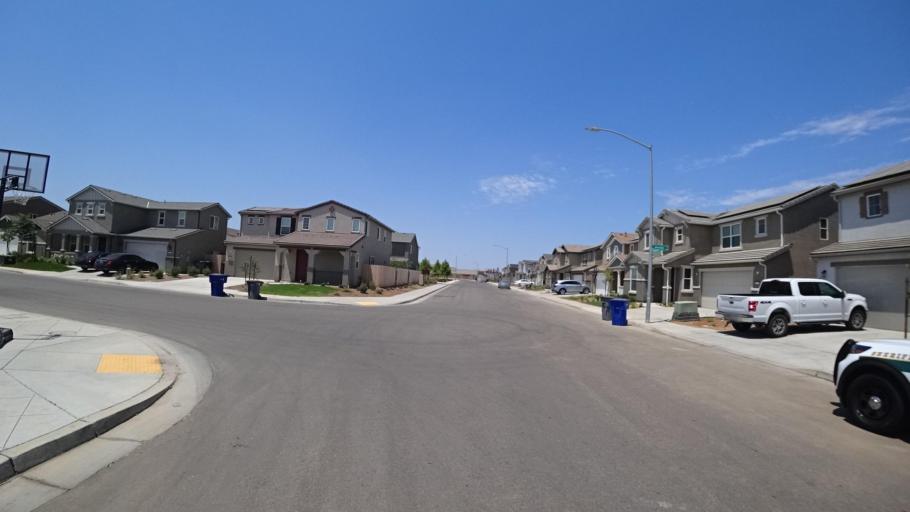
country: US
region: California
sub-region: Fresno County
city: Tarpey Village
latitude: 36.7778
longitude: -119.6562
